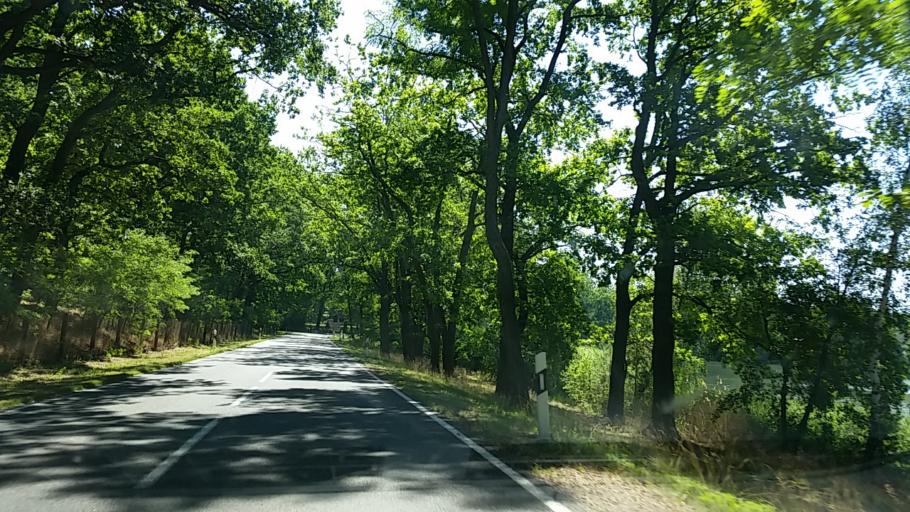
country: DE
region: Saxony-Anhalt
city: Pretzsch
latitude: 51.6871
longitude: 12.7979
